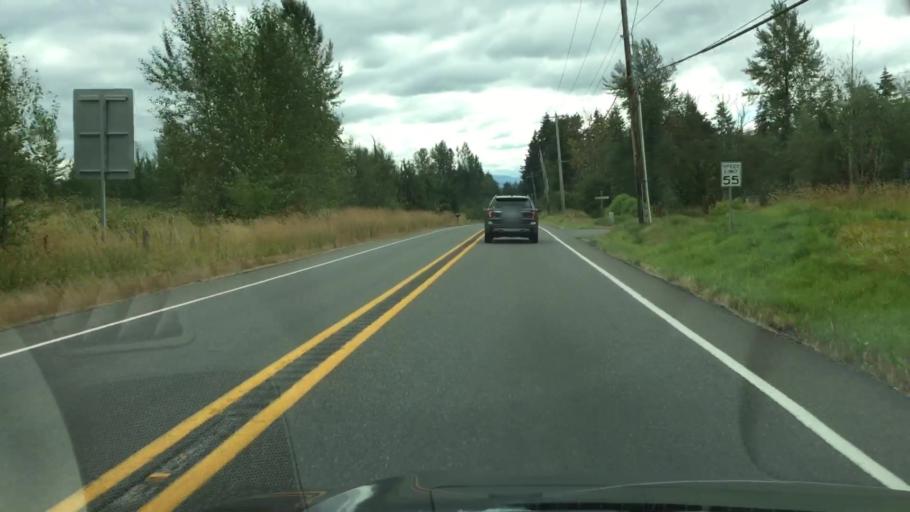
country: US
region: Washington
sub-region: Pierce County
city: Graham
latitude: 47.0144
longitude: -122.2964
